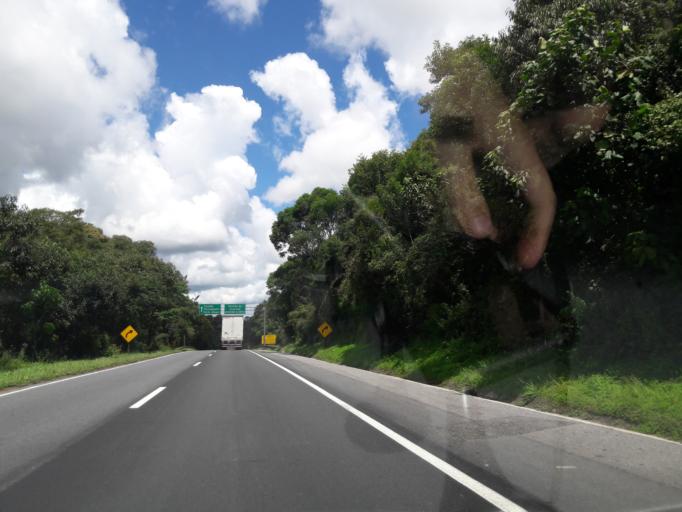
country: BR
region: Parana
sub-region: Campina Grande Do Sul
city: Campina Grande do Sul
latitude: -25.3003
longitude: -48.9421
